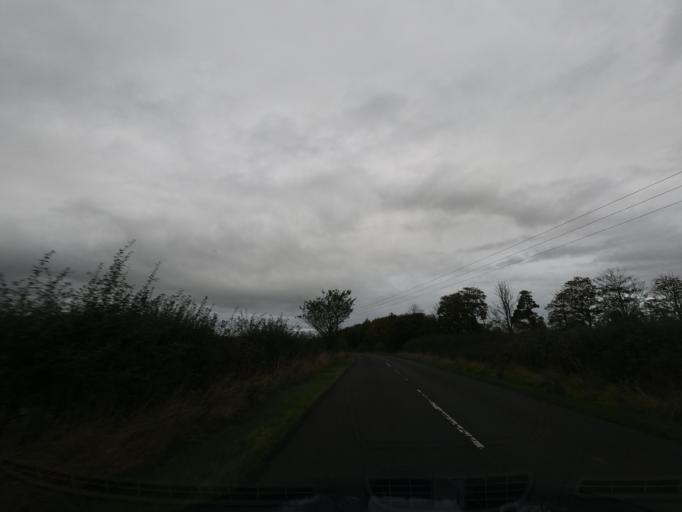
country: GB
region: England
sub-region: Northumberland
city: Ford
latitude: 55.6888
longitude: -2.0828
